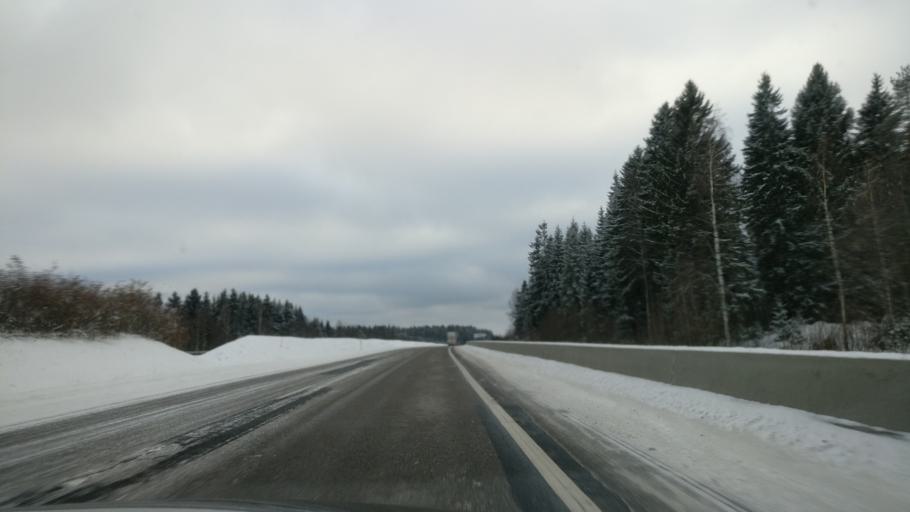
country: FI
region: Paijanne Tavastia
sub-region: Lahti
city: Nastola
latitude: 61.0867
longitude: 25.8944
